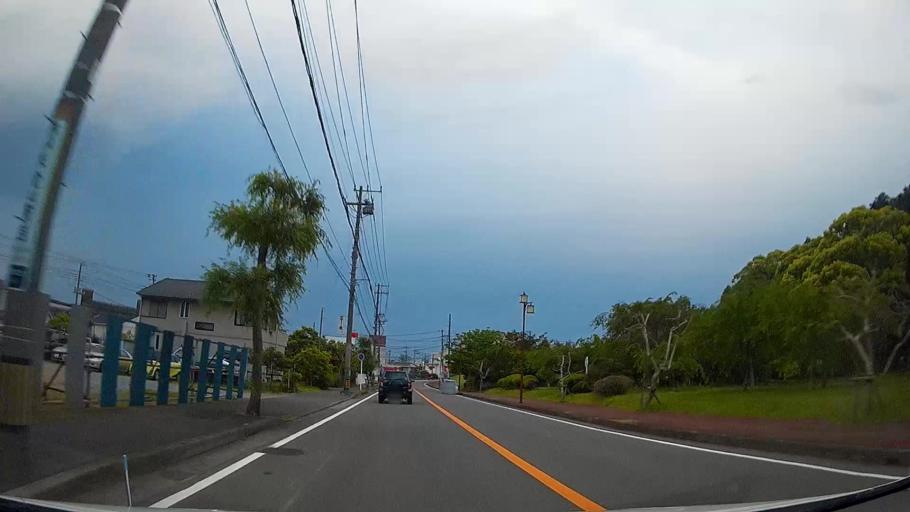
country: JP
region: Kanagawa
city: Yugawara
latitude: 35.1423
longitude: 139.1089
